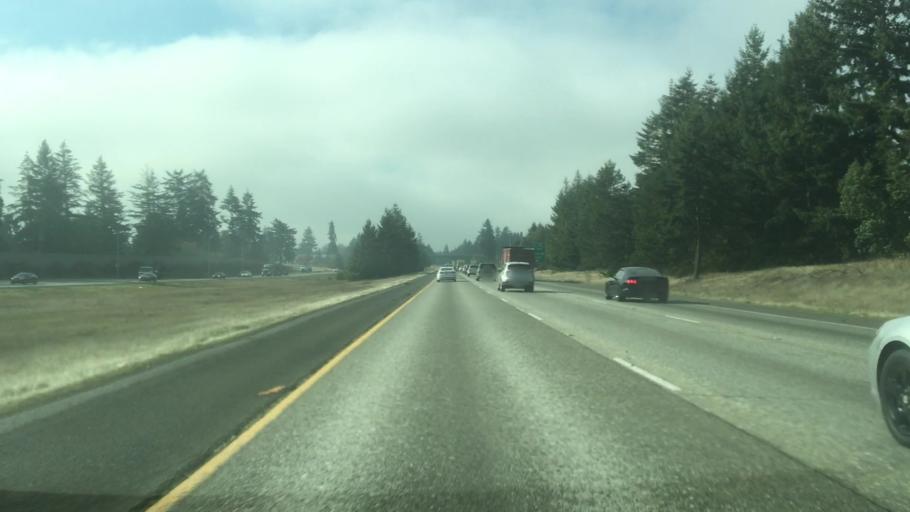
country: US
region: Washington
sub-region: Thurston County
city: Tanglewilde-Thompson Place
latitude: 47.0646
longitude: -122.7562
